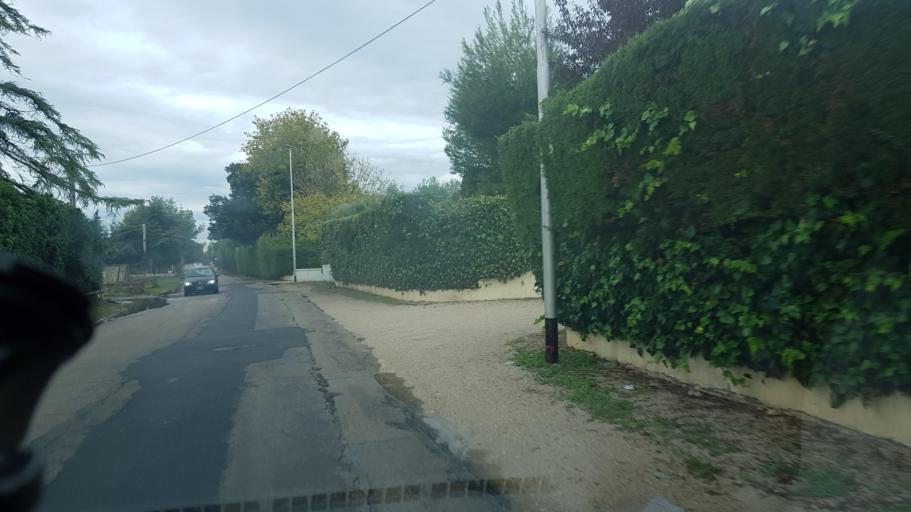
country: IT
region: Apulia
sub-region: Provincia di Lecce
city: Carmiano
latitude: 40.3524
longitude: 18.0344
